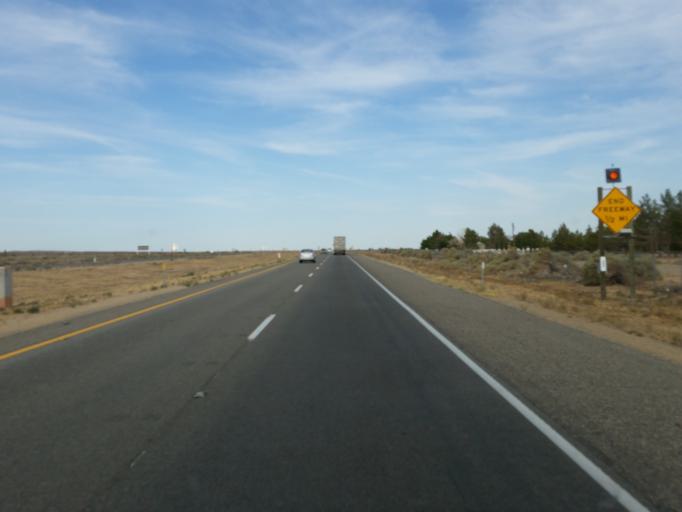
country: US
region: California
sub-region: Kern County
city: Boron
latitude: 35.0101
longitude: -117.6400
